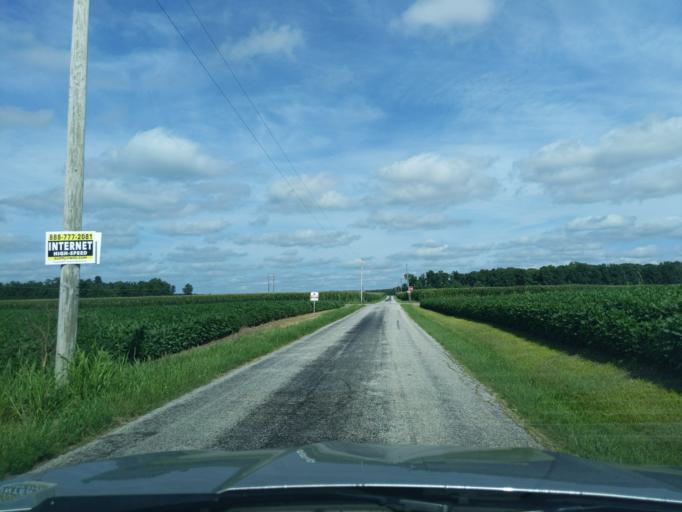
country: US
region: Indiana
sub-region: Ripley County
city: Osgood
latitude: 39.2352
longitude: -85.3764
